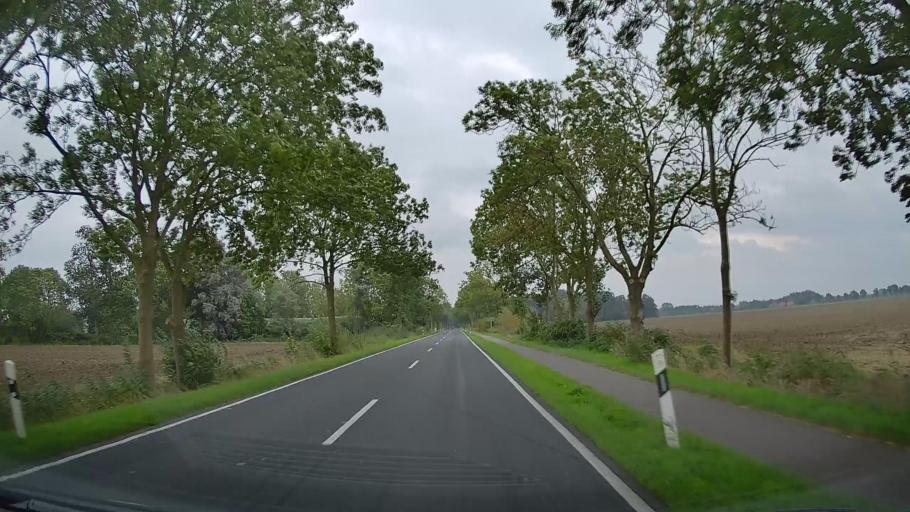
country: DE
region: Lower Saxony
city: Wischhafen
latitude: 53.8045
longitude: 9.3146
